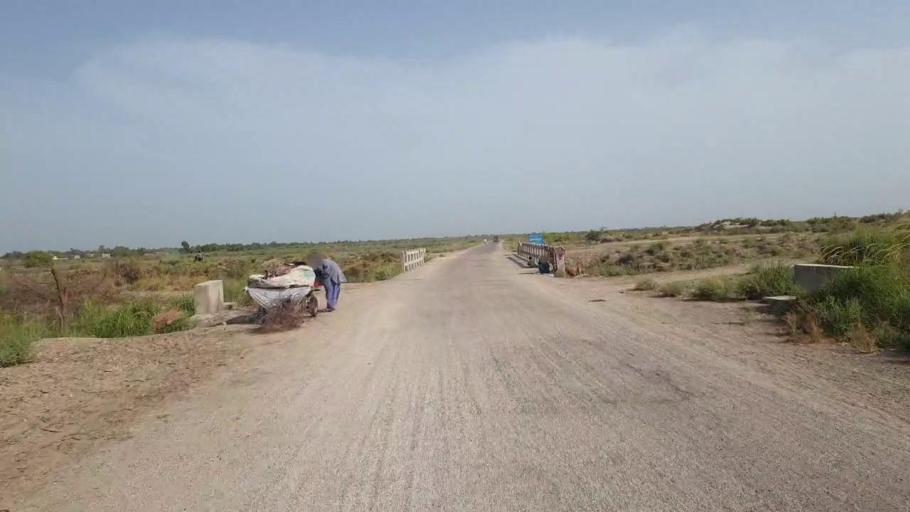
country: PK
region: Sindh
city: Sakrand
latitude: 26.2778
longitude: 68.2710
